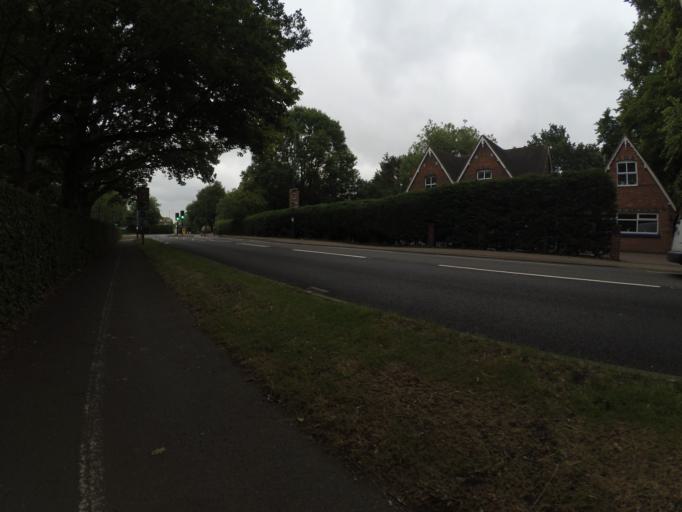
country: GB
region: England
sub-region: Warwickshire
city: Rugby
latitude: 52.3605
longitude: -1.2693
